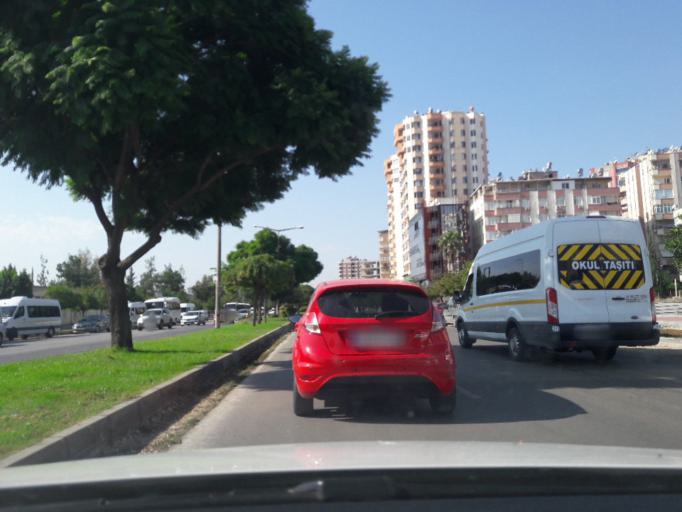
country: TR
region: Adana
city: Adana
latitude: 37.0063
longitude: 35.3217
